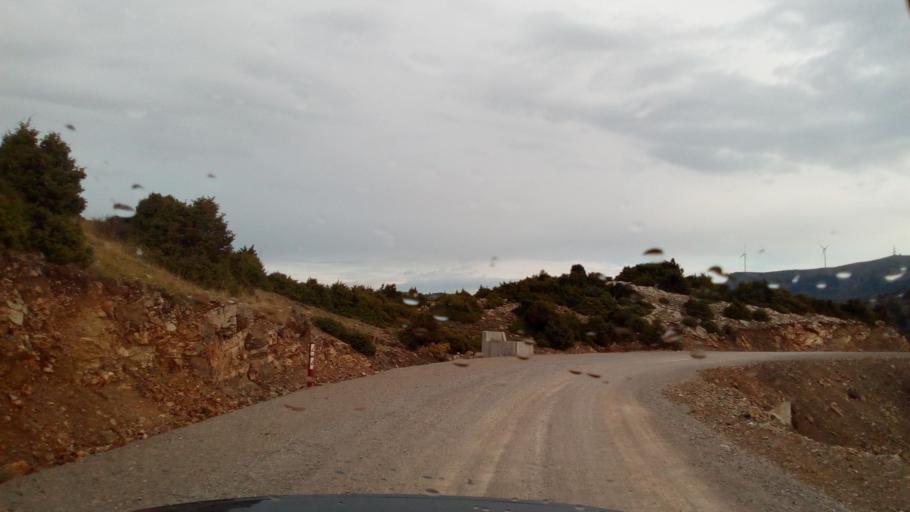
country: GR
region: West Greece
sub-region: Nomos Achaias
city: Kamarai
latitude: 38.4305
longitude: 22.0499
